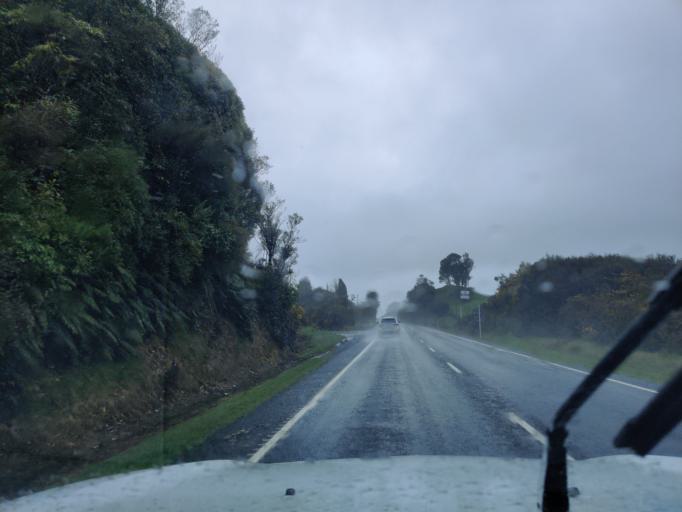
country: NZ
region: Bay of Plenty
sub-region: Rotorua District
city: Rotorua
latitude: -38.0395
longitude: 176.0542
